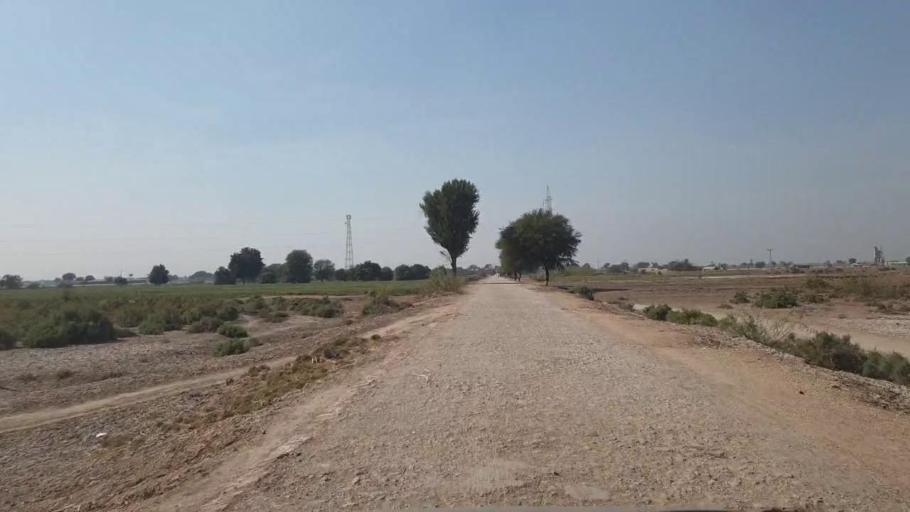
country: PK
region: Sindh
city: Chambar
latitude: 25.3320
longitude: 68.8025
